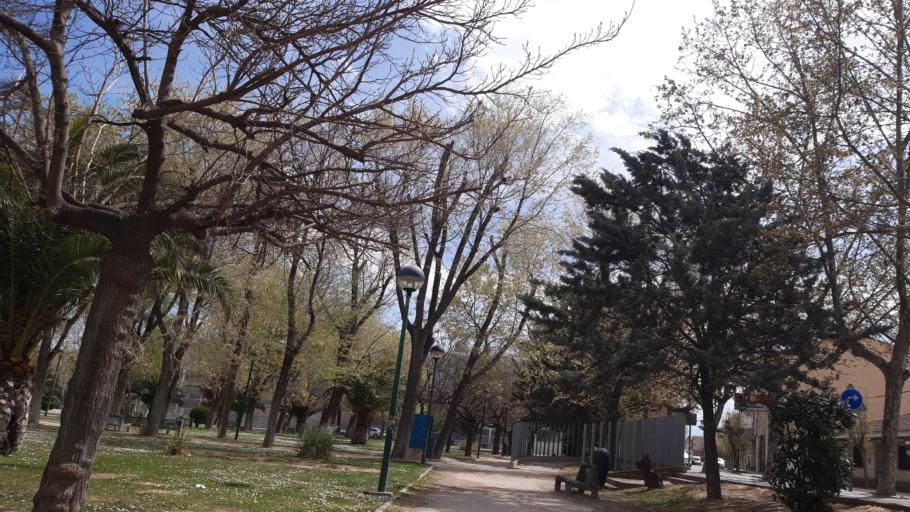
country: ES
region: Aragon
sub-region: Provincia de Zaragoza
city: Utebo
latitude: 41.7124
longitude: -1.0034
